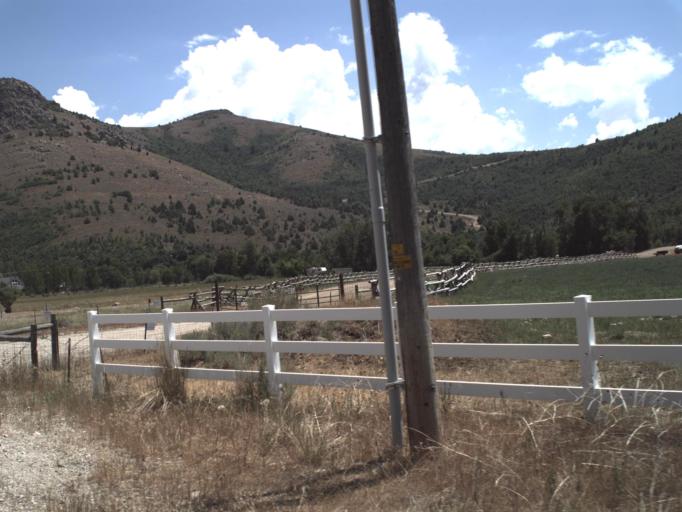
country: US
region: Utah
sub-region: Weber County
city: Wolf Creek
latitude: 41.2610
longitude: -111.7083
